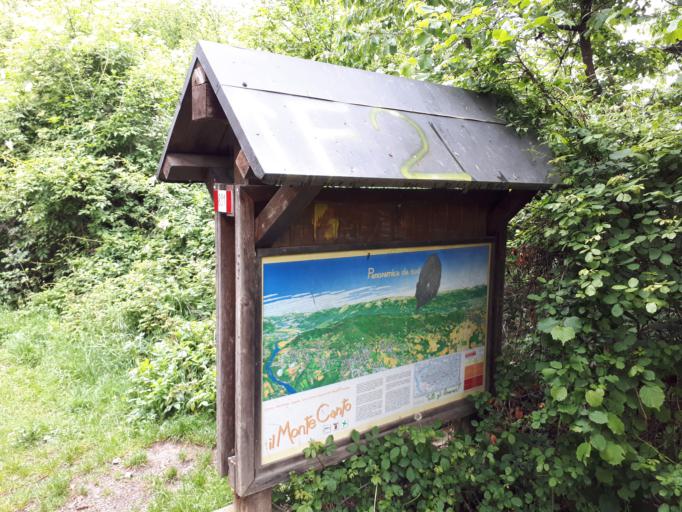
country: IT
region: Lombardy
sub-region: Provincia di Bergamo
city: Pontida
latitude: 45.7227
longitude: 9.4946
